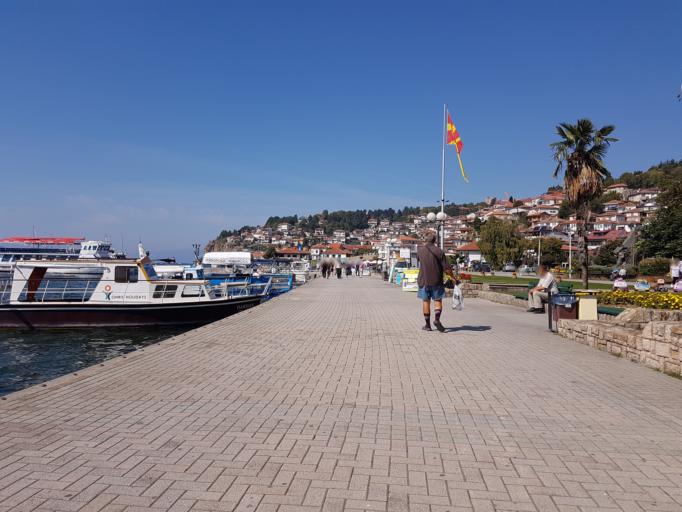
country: MK
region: Ohrid
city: Ohrid
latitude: 41.1118
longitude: 20.8007
